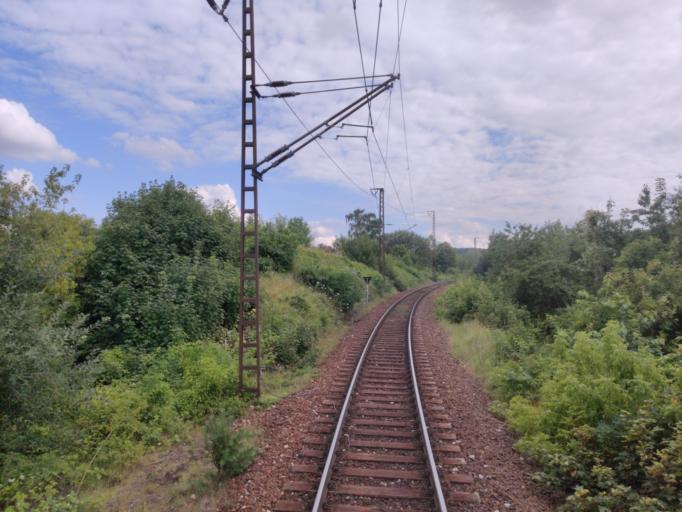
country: DE
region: Saxony-Anhalt
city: Blankenburg
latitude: 51.7988
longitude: 10.9425
